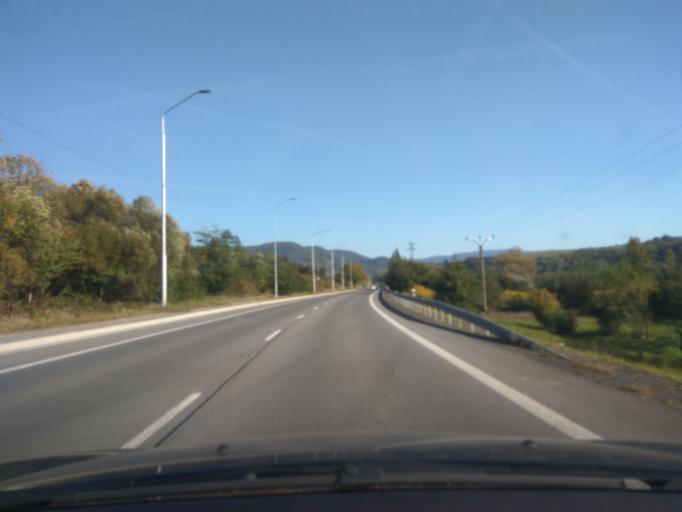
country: SK
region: Nitriansky
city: Handlova
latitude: 48.7743
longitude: 18.7367
